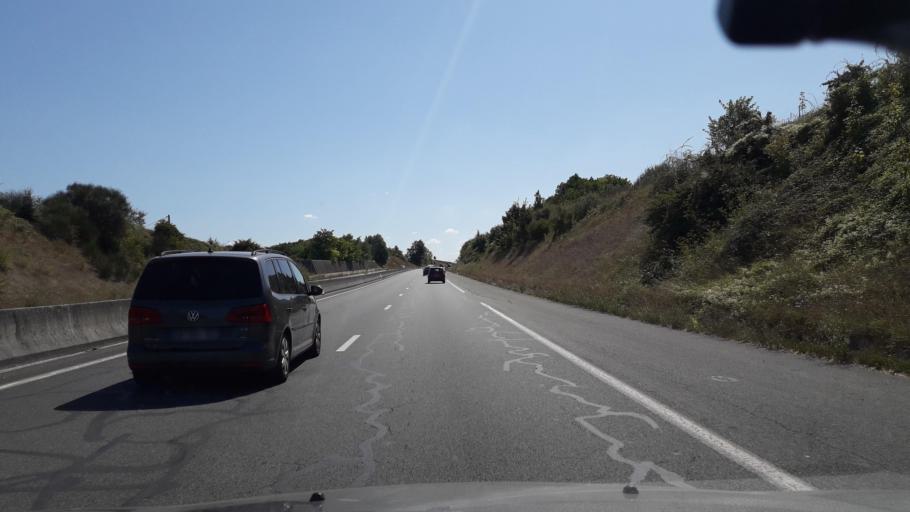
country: FR
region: Poitou-Charentes
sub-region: Departement de la Charente
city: Saint-Yrieix-sur-Charente
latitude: 45.6878
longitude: 0.1091
